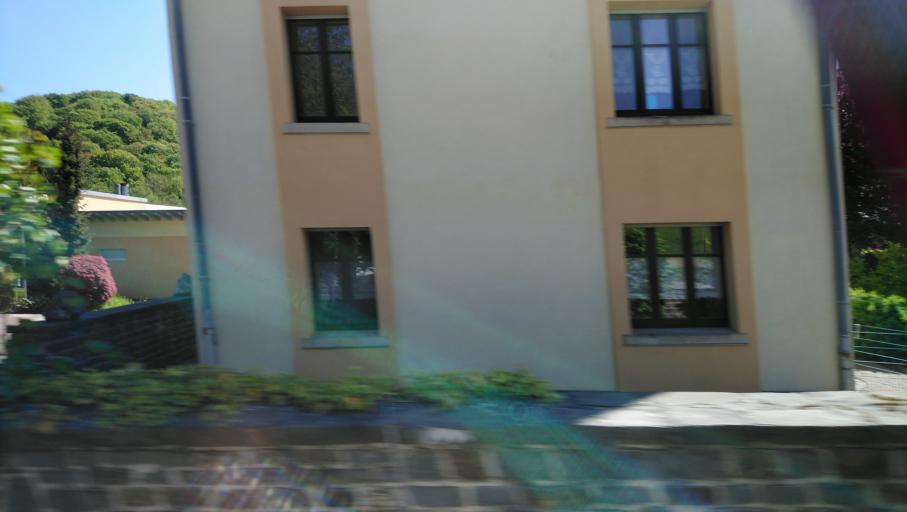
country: LU
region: Diekirch
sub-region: Canton de Vianden
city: Tandel
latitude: 49.8940
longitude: 6.1819
